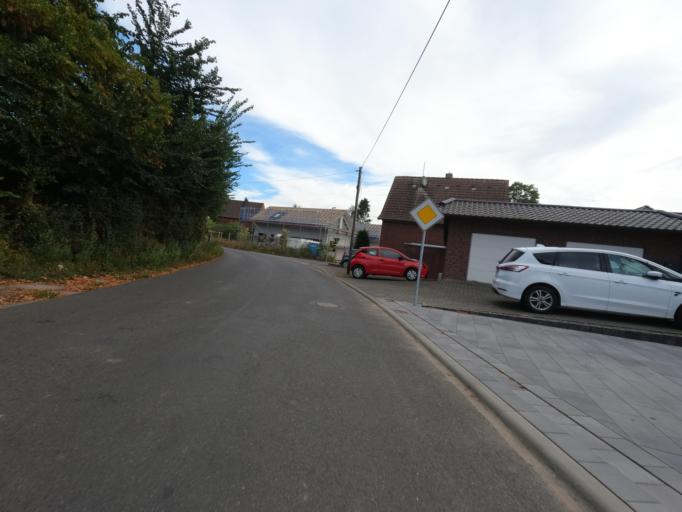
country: NL
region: Limburg
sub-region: Gemeente Roerdalen
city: Vlodrop
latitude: 51.1218
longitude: 6.0986
